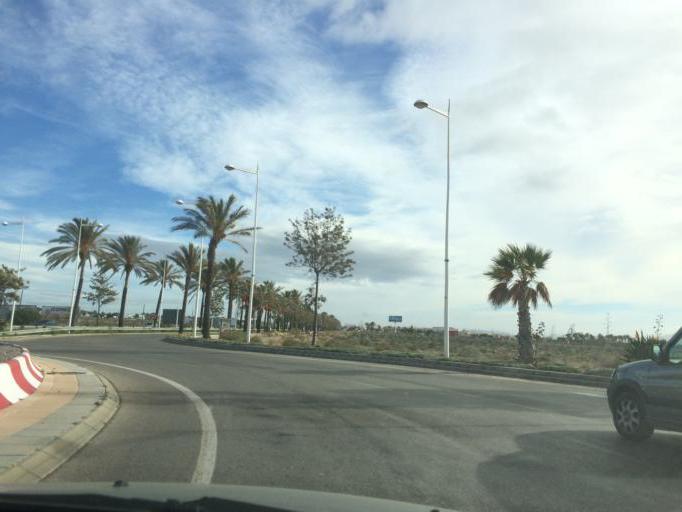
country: ES
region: Andalusia
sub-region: Provincia de Almeria
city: Retamar
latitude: 36.8519
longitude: -2.3203
